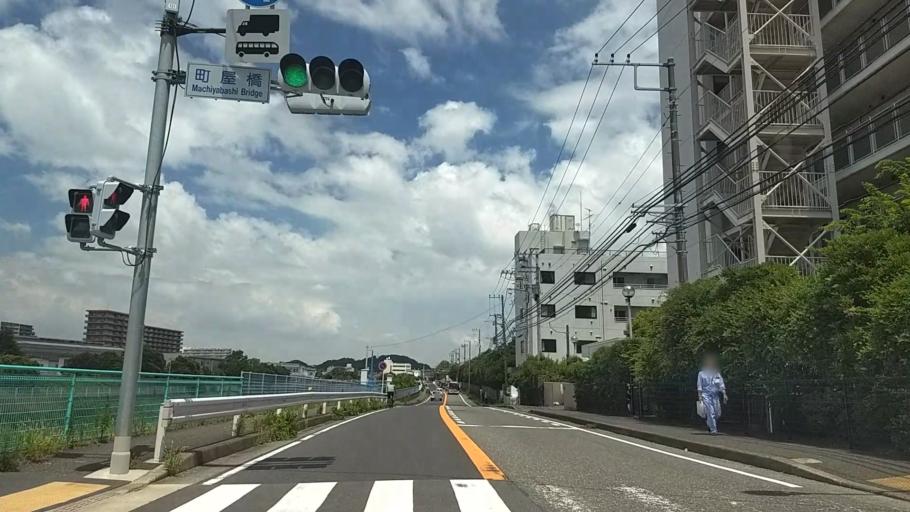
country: JP
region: Kanagawa
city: Fujisawa
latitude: 35.3394
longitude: 139.5152
